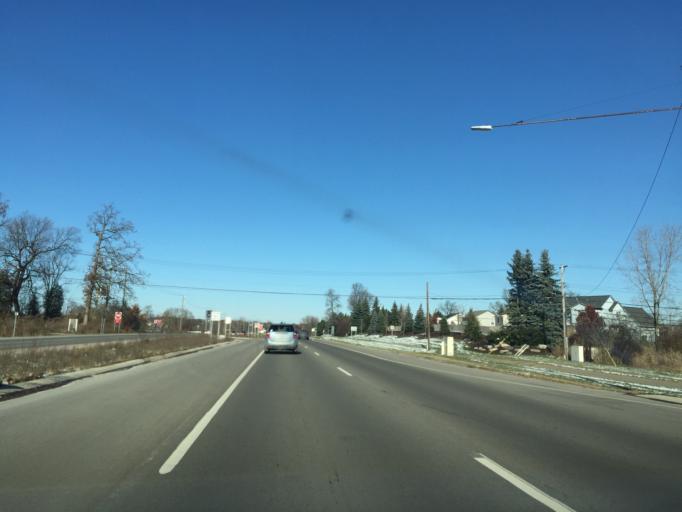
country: US
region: Michigan
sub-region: Oakland County
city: Lake Orion
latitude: 42.7451
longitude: -83.2460
